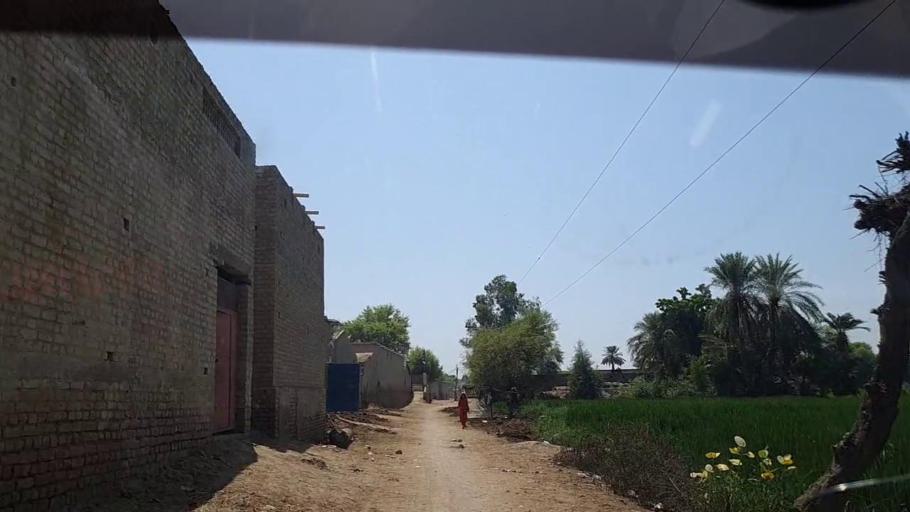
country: PK
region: Sindh
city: Ghauspur
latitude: 28.1637
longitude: 69.1252
